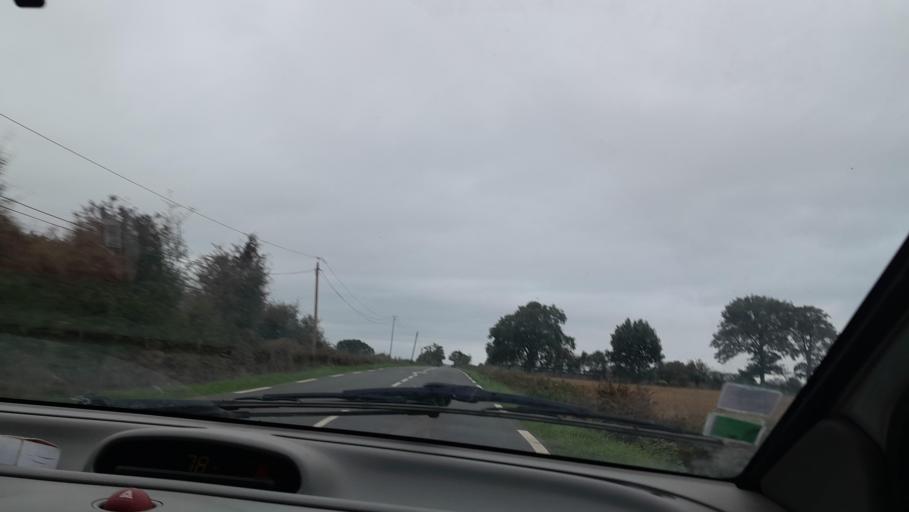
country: FR
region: Pays de la Loire
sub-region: Departement de la Loire-Atlantique
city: Saint-Mars-la-Jaille
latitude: 47.6315
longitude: -1.2010
